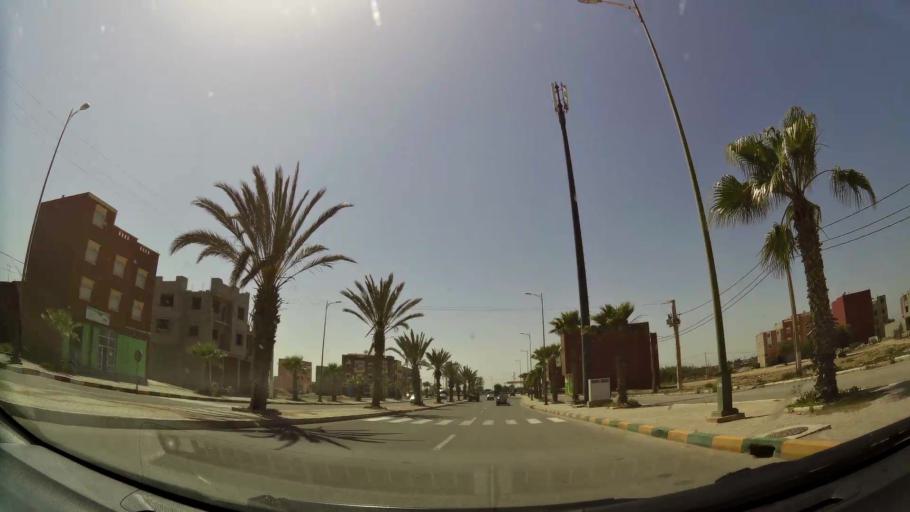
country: MA
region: Souss-Massa-Draa
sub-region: Inezgane-Ait Mellou
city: Inezgane
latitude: 30.3128
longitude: -9.5030
